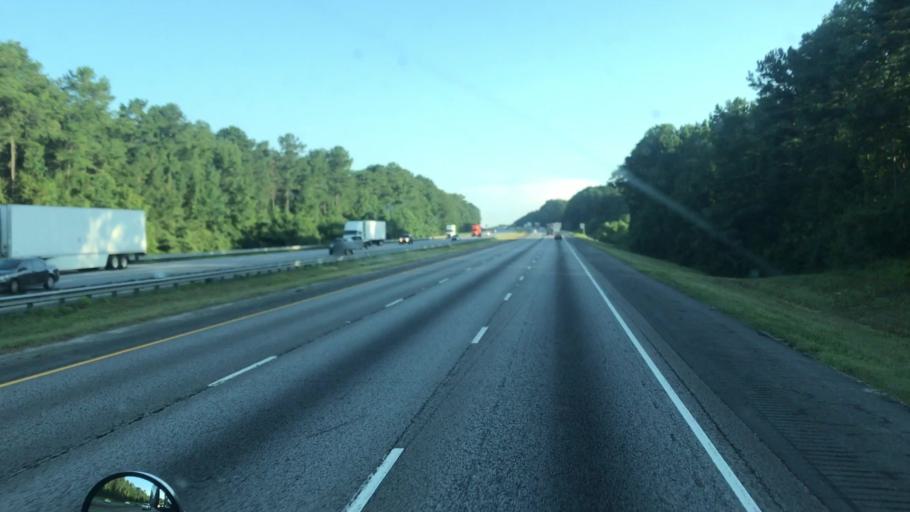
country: US
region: Georgia
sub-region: Henry County
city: Locust Grove
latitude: 33.3018
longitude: -84.1130
